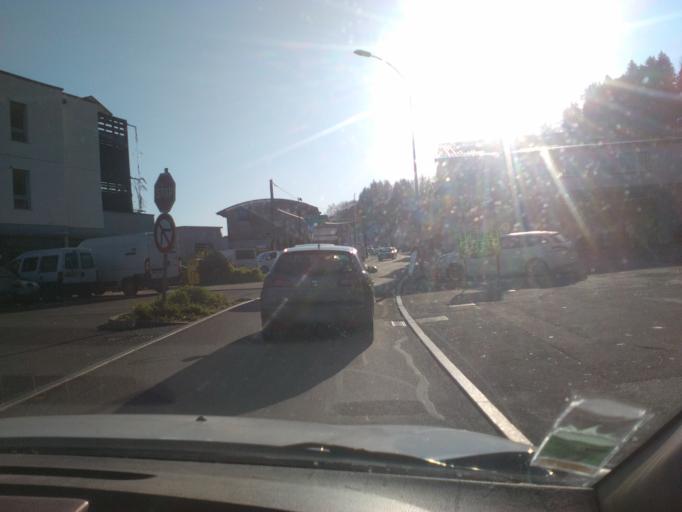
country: FR
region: Lorraine
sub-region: Departement des Vosges
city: Saint-Etienne-les-Remiremont
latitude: 48.0120
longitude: 6.6012
